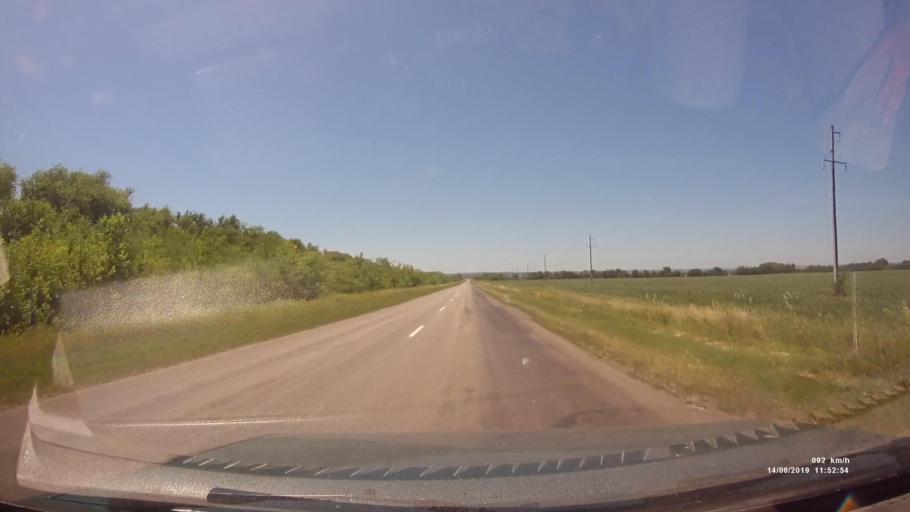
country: RU
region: Rostov
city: Kazanskaya
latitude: 49.8320
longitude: 41.2204
